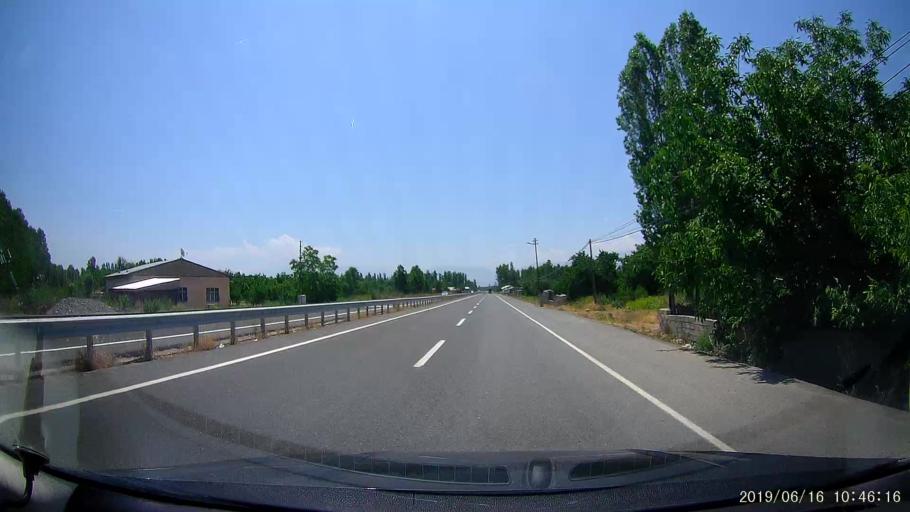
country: AM
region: Armavir
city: Shenavan
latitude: 40.0235
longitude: 43.8782
